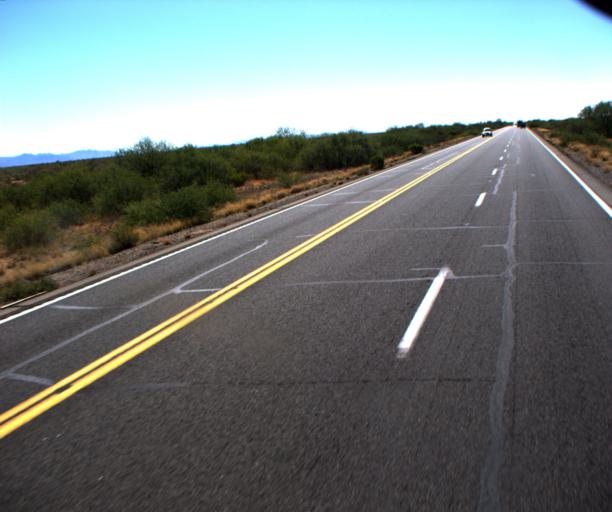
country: US
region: Arizona
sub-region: Yavapai County
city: Congress
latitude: 34.1541
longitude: -112.9948
